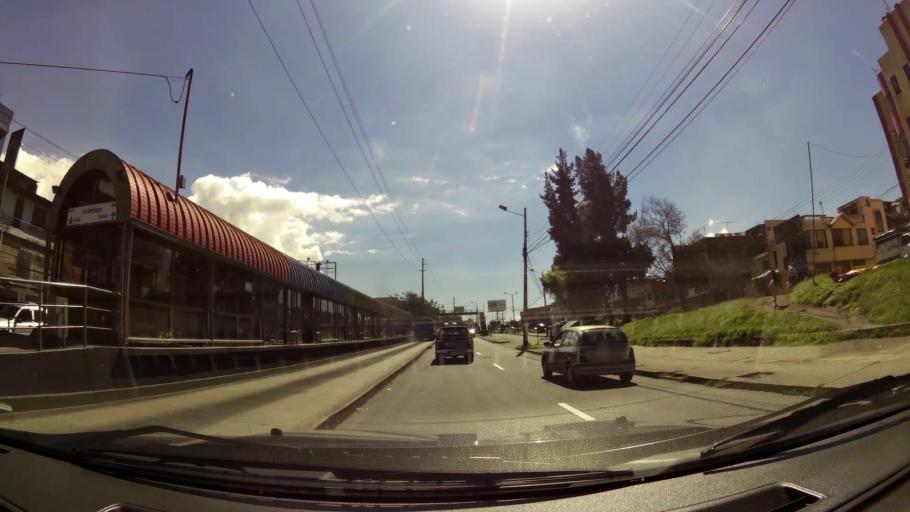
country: EC
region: Pichincha
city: Quito
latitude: -0.2533
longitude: -78.5399
